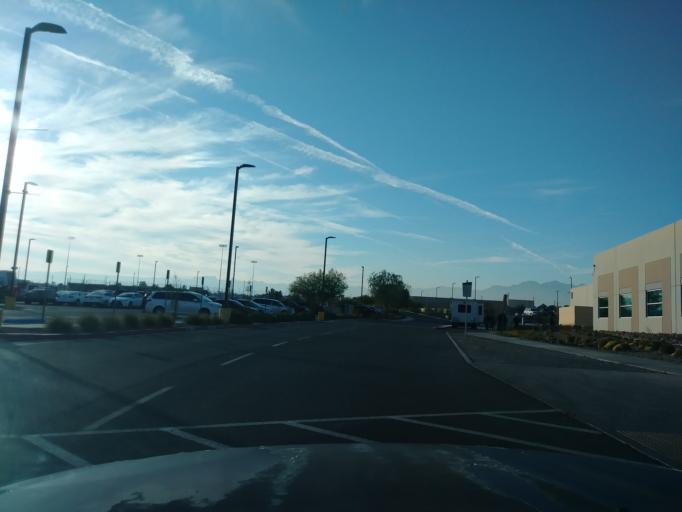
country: US
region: Nevada
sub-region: Clark County
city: Spring Valley
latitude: 36.1539
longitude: -115.2315
